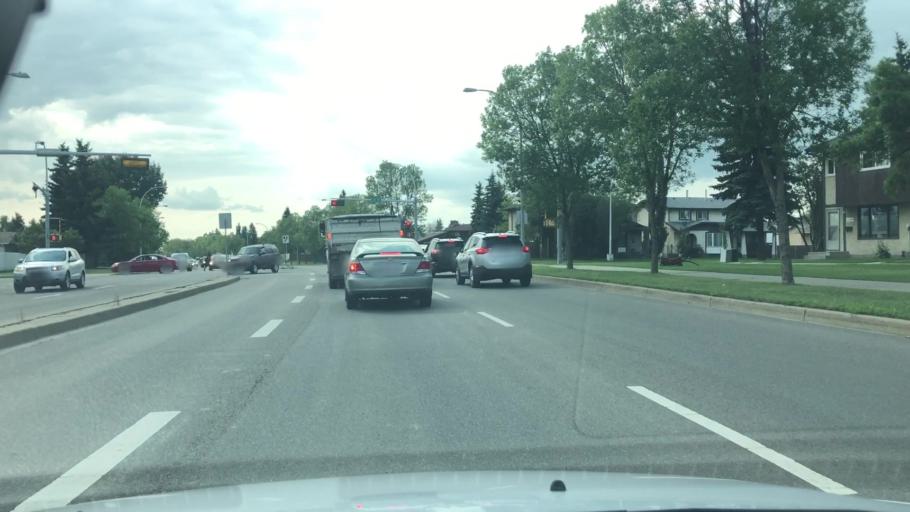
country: CA
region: Alberta
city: Edmonton
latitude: 53.6169
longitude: -113.5296
